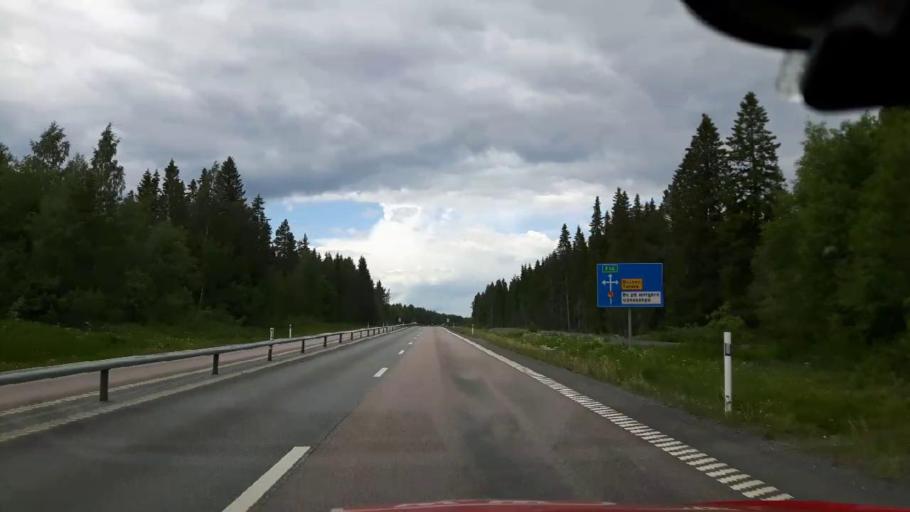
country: SE
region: Jaemtland
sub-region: OEstersunds Kommun
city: Ostersund
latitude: 63.2532
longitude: 14.5758
